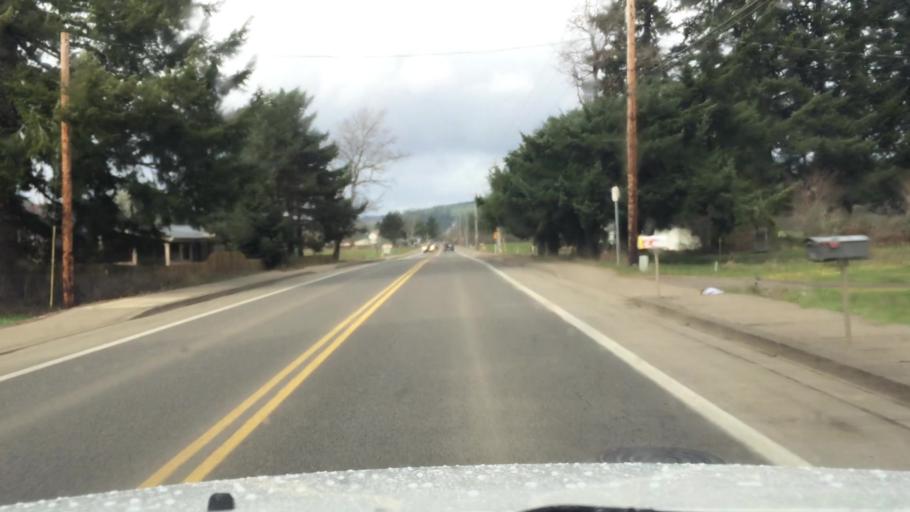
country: US
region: Oregon
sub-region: Polk County
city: Grand Ronde
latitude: 45.0717
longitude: -123.6119
